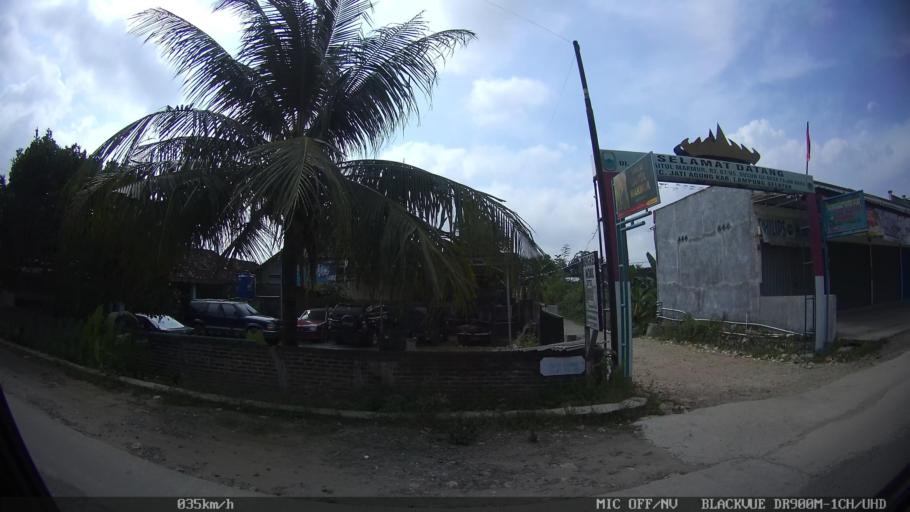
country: ID
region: Lampung
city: Kedaton
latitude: -5.3443
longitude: 105.2686
